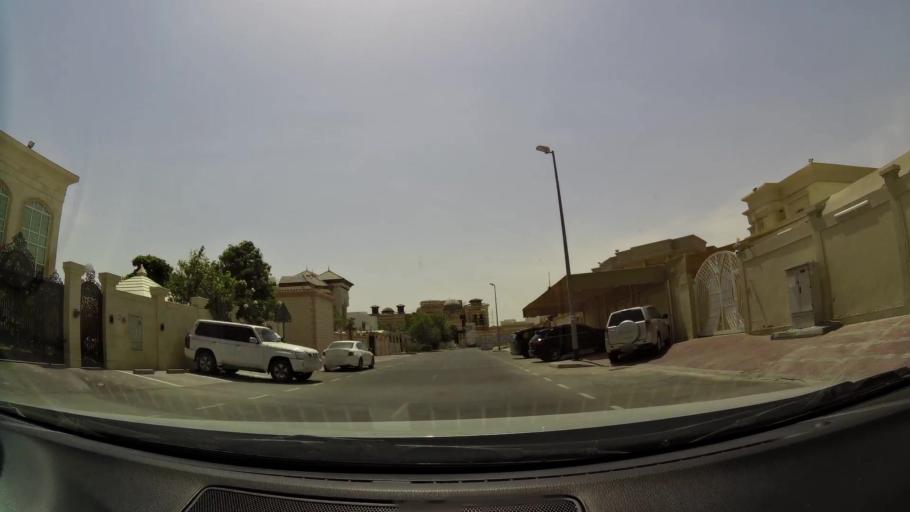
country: AE
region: Ash Shariqah
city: Sharjah
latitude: 25.1814
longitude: 55.4196
